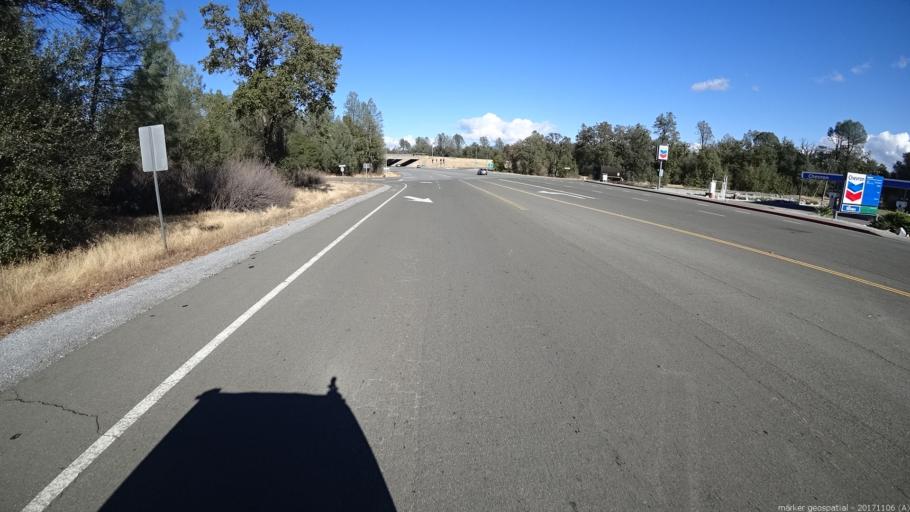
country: US
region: California
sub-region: Shasta County
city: Redding
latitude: 40.6186
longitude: -122.3186
